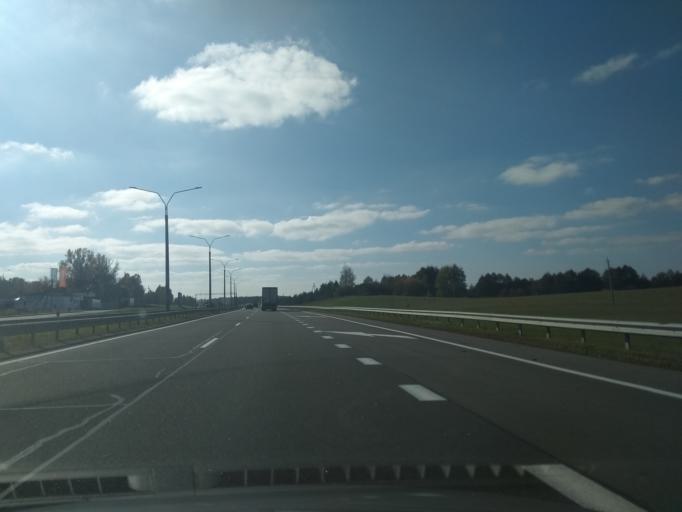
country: BY
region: Brest
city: Baranovichi
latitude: 53.1265
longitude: 25.9072
